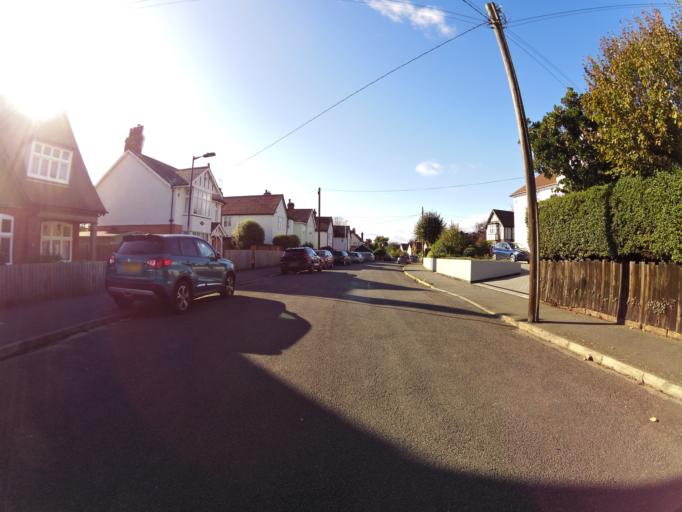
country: GB
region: England
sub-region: Suffolk
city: Felixstowe
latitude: 51.9658
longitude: 1.3629
